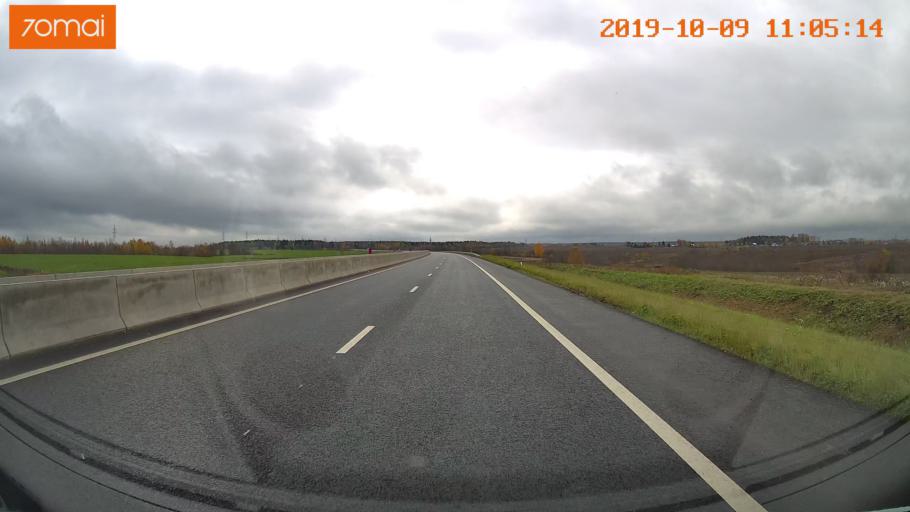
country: RU
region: Vologda
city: Molochnoye
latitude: 59.2027
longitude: 39.7600
